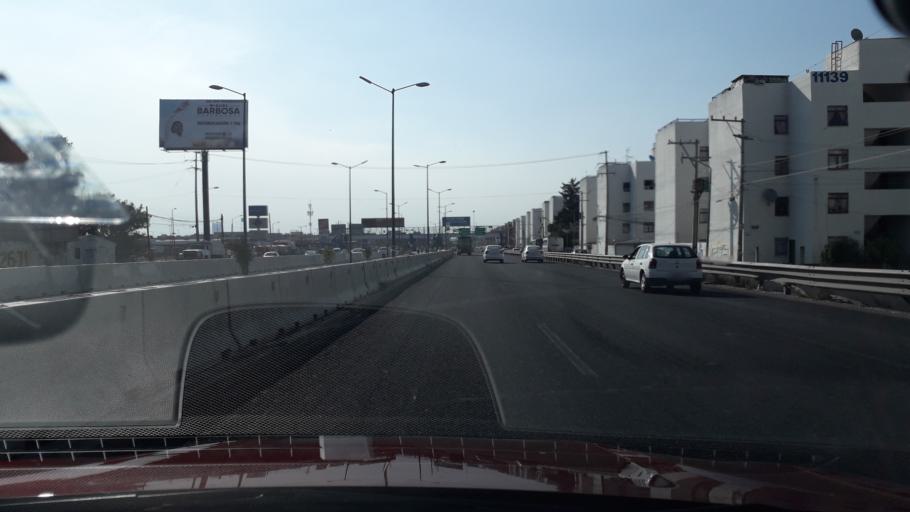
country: MX
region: Puebla
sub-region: Puebla
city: El Capulo (La Quebradora)
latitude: 18.9873
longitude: -98.2364
